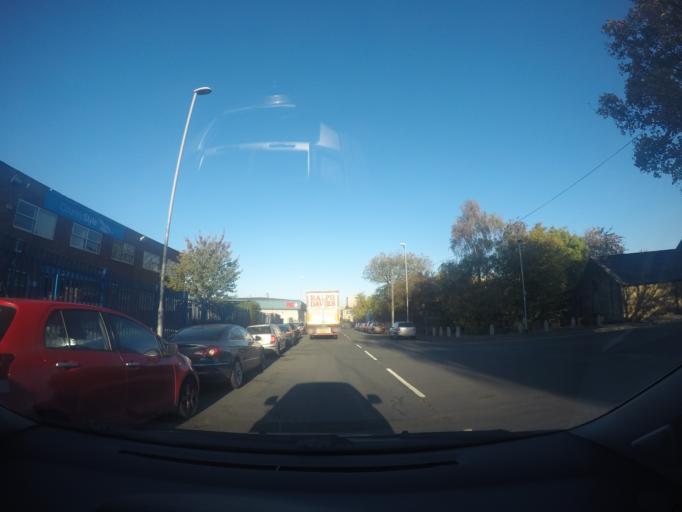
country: GB
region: England
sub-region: City and Borough of Leeds
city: Leeds
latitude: 53.7967
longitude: -1.5212
